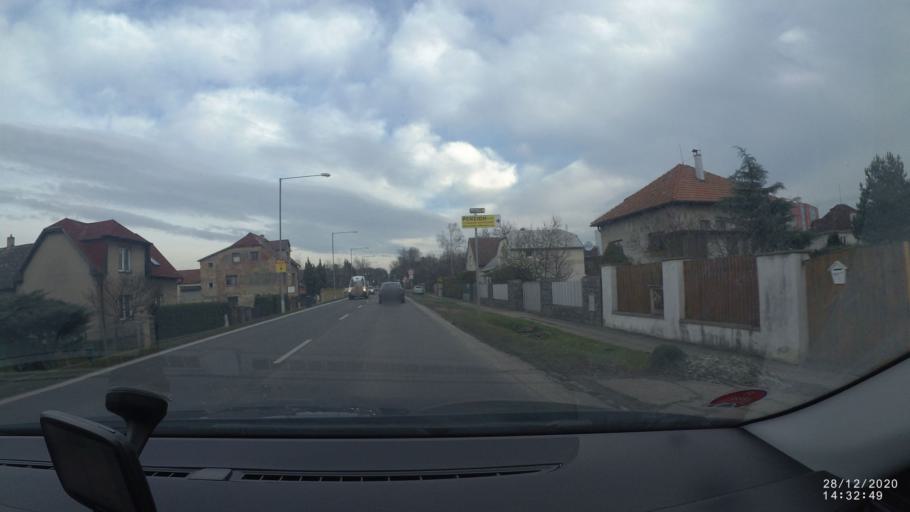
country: CZ
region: Central Bohemia
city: Sestajovice
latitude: 50.0733
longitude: 14.6786
